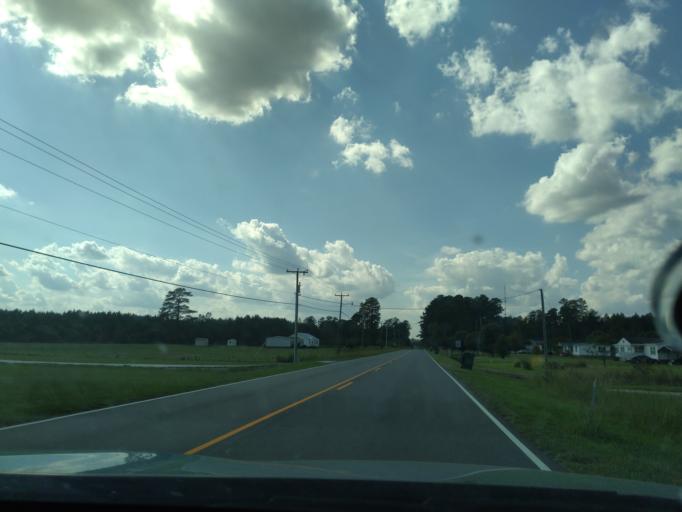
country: US
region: North Carolina
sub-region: Pitt County
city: Bethel
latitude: 35.8238
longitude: -77.3152
